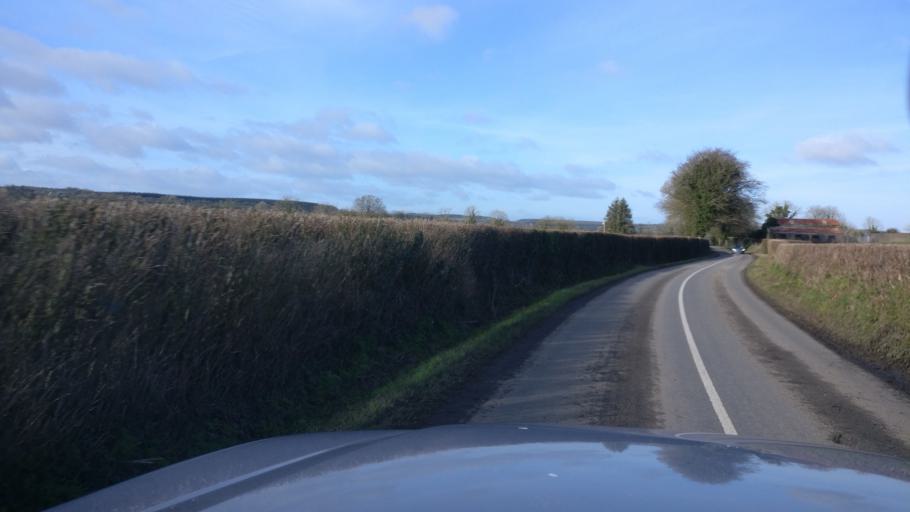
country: IE
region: Leinster
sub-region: Kilkenny
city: Castlecomer
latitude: 52.8770
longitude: -7.1622
